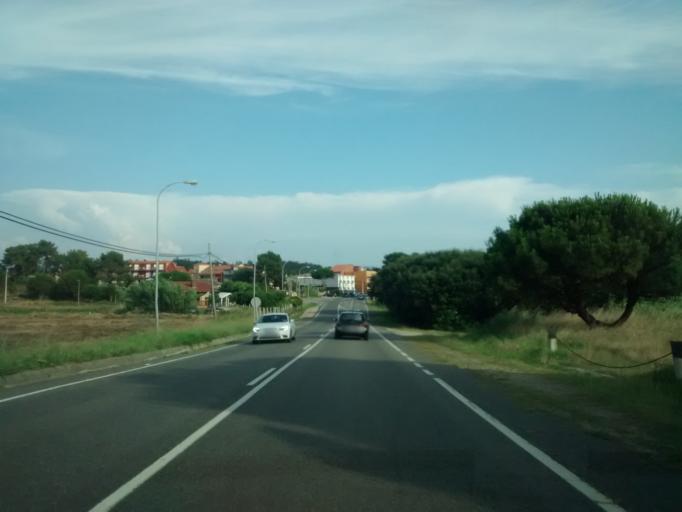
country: ES
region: Galicia
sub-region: Provincia de Pontevedra
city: Sanxenxo
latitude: 42.4000
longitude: -8.8470
